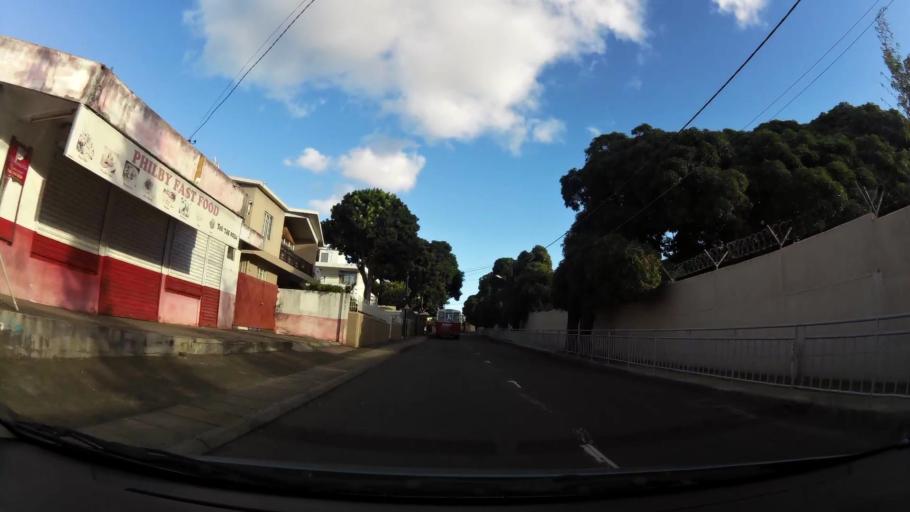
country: MU
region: Plaines Wilhems
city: Ebene
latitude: -20.2295
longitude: 57.4633
